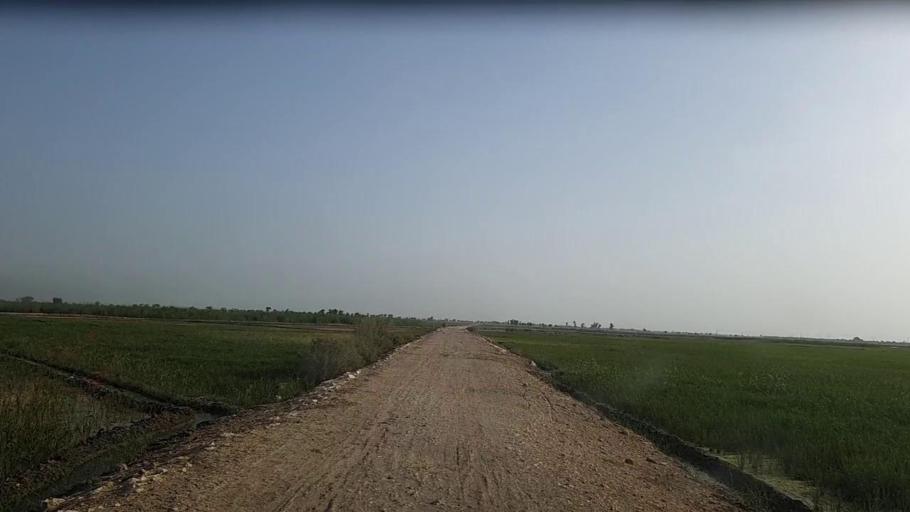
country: PK
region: Sindh
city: Sita Road
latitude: 27.1085
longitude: 67.8909
